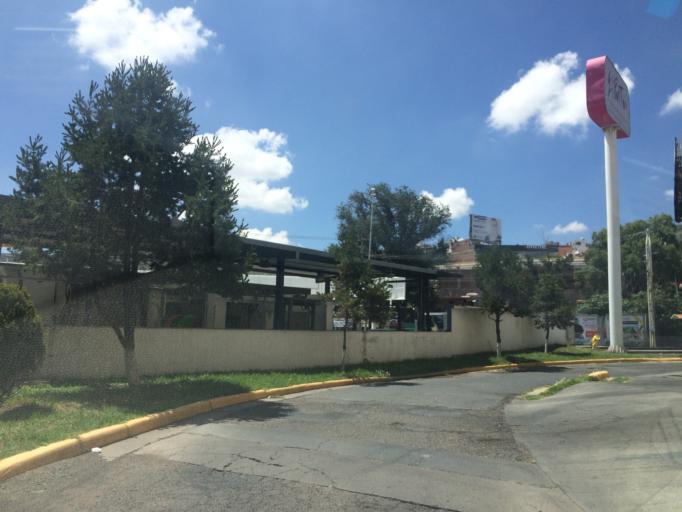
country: MX
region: Zacatecas
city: Guadalupe
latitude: 22.7623
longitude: -102.5488
